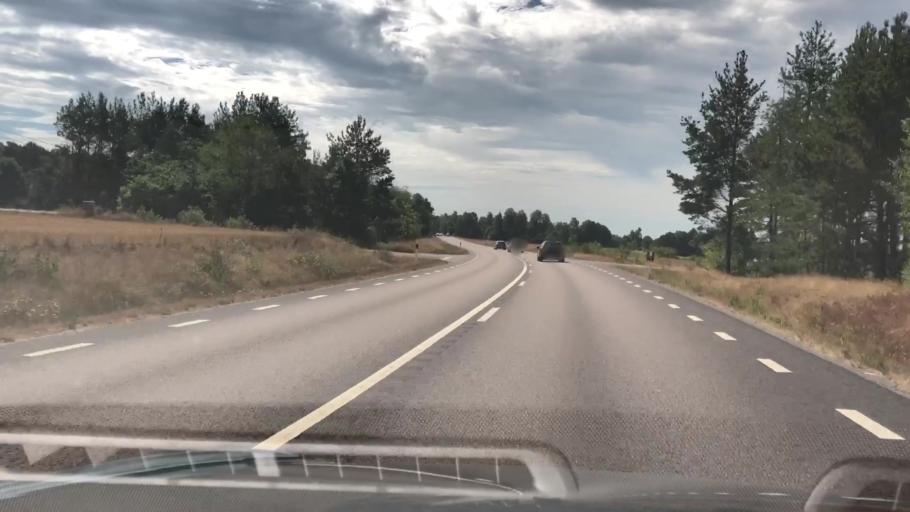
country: SE
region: Kalmar
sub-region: Torsas Kommun
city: Torsas
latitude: 56.3495
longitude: 16.0485
